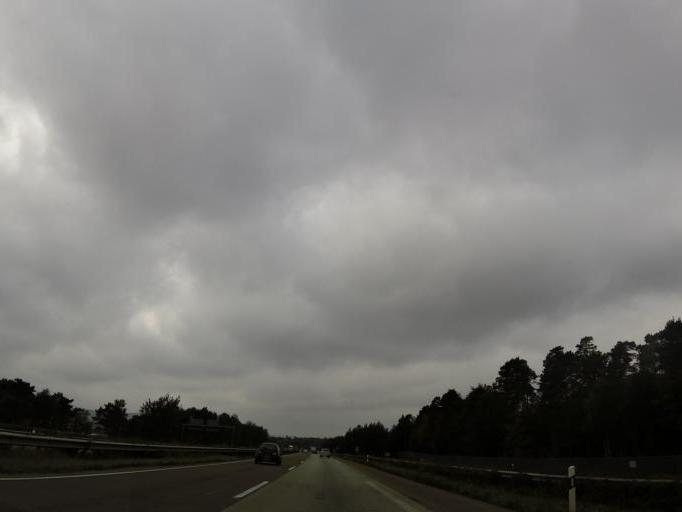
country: DE
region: Rheinland-Pfalz
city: Katzweiler
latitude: 49.4473
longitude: 7.7009
